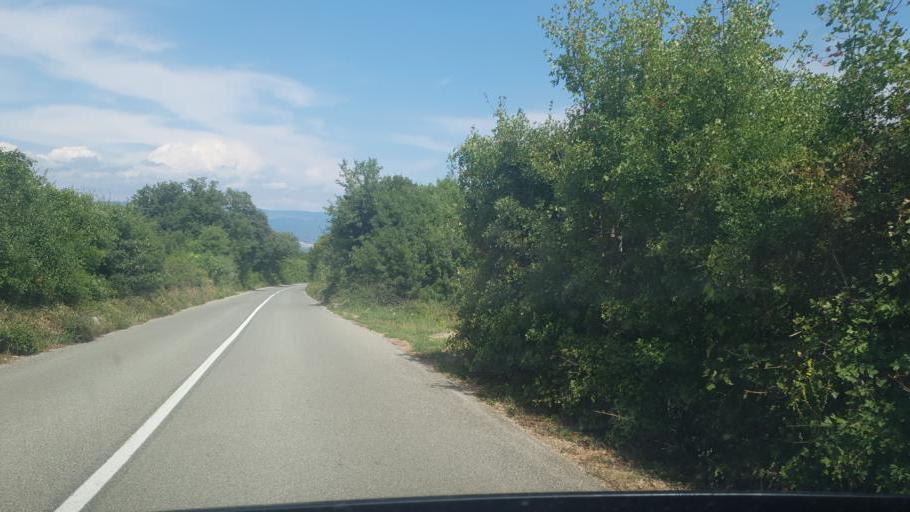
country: HR
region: Primorsko-Goranska
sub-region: Grad Crikvenica
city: Crikvenica
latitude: 45.1077
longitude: 14.6363
